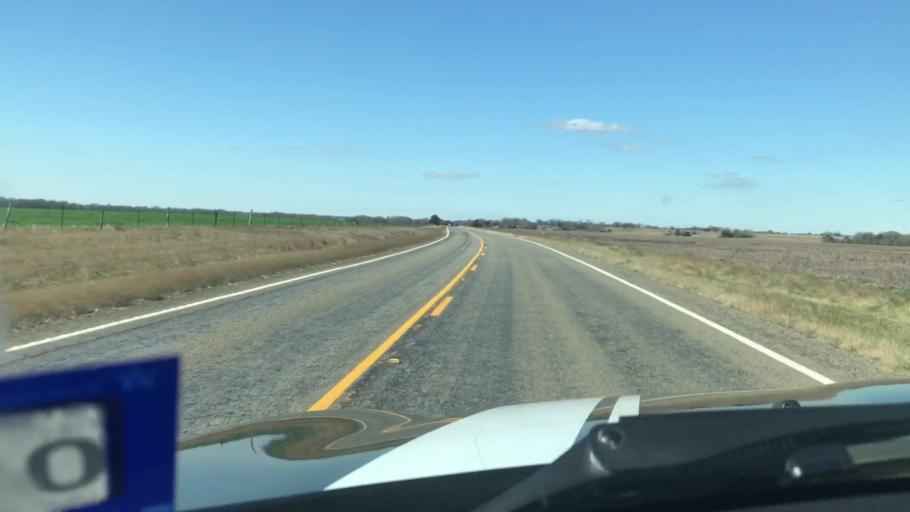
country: US
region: Texas
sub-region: Robertson County
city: Calvert
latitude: 30.8725
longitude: -96.7173
